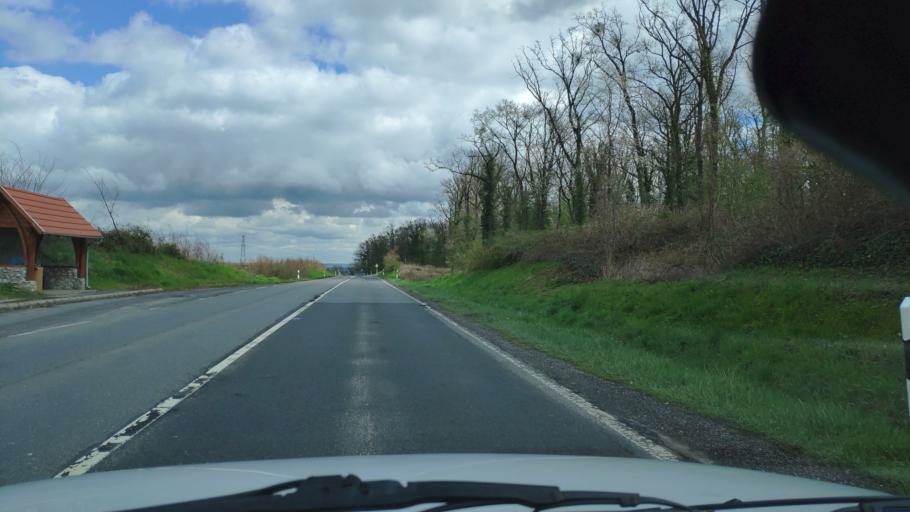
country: HU
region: Zala
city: Zalakomar
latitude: 46.5065
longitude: 17.1031
